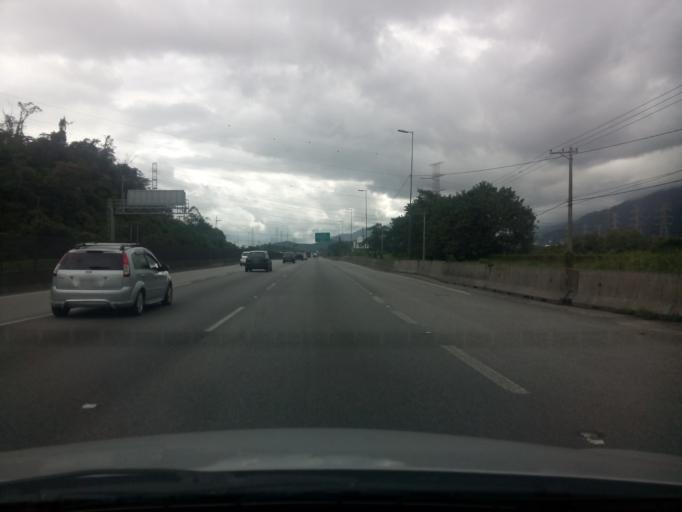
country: BR
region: Sao Paulo
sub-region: Cubatao
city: Cubatao
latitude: -23.8577
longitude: -46.4109
